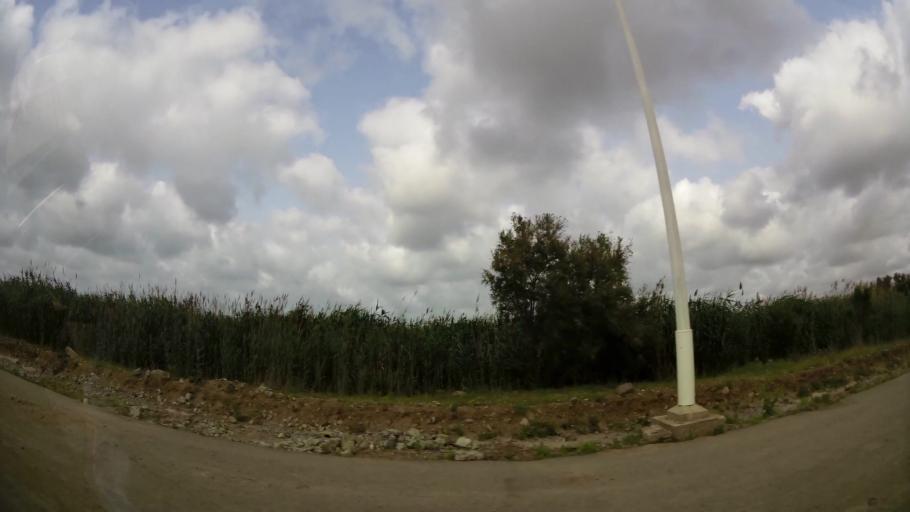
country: MA
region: Oriental
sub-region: Nador
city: Nador
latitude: 35.1549
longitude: -2.9069
